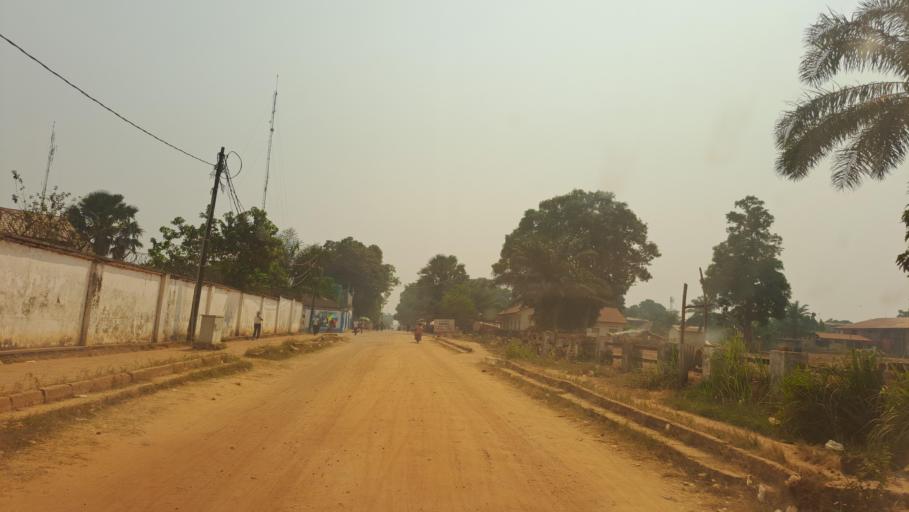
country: CD
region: Kasai-Occidental
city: Kananga
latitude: -5.9023
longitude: 22.4059
